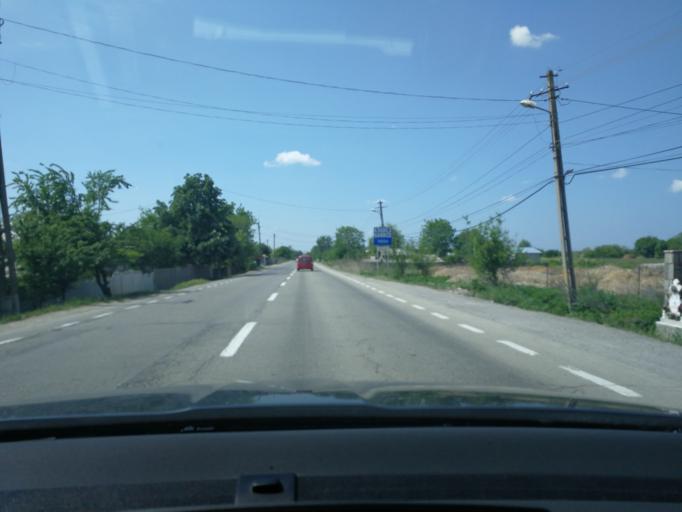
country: RO
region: Prahova
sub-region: Comuna Targsoru Vechi
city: Targsoru Vechi
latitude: 44.8741
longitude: 25.9390
